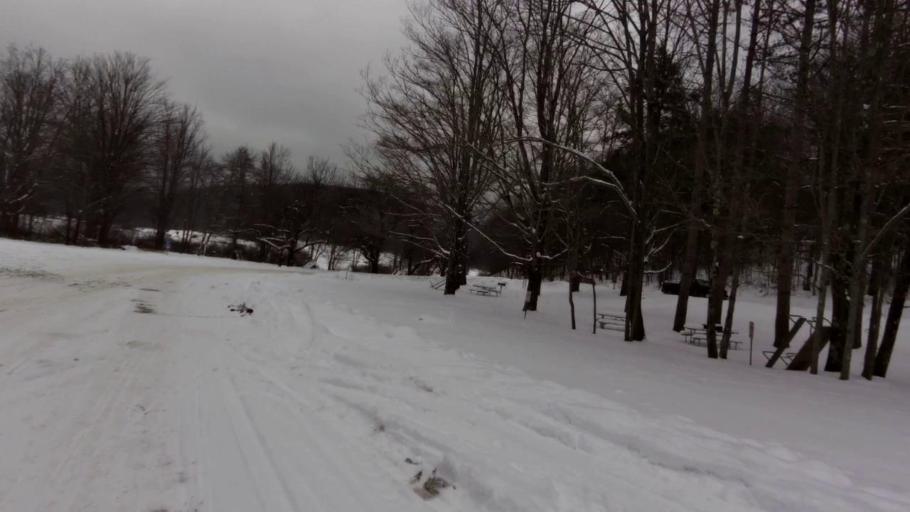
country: US
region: New York
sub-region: Cattaraugus County
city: Salamanca
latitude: 42.0988
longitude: -78.7463
